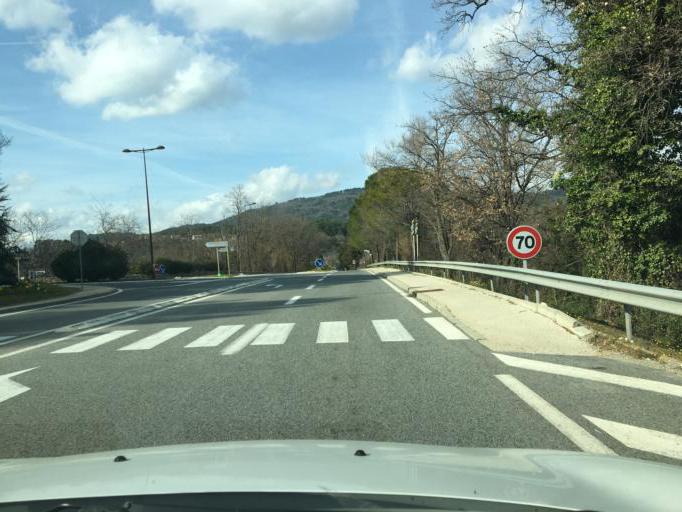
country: FR
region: Provence-Alpes-Cote d'Azur
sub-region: Departement du Var
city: Figanieres
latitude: 43.5652
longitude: 6.5083
